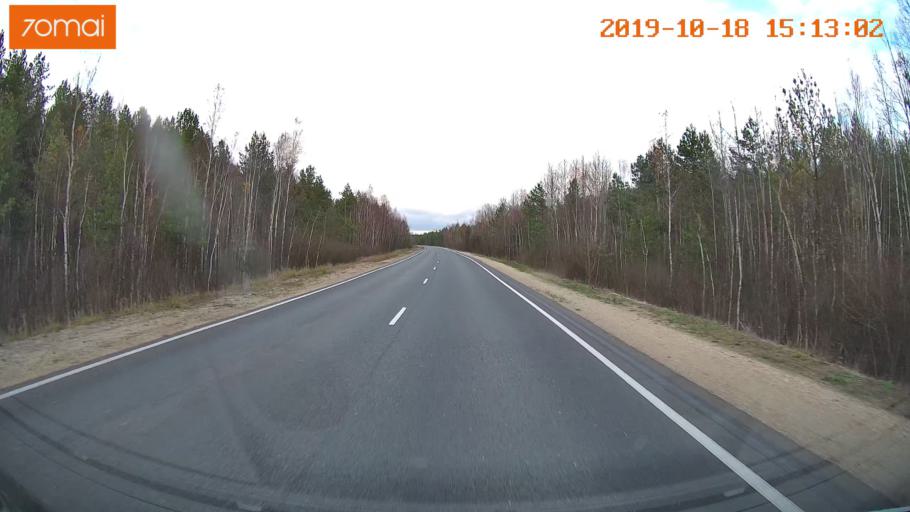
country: RU
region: Vladimir
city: Gus'-Khrustal'nyy
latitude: 55.5813
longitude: 40.7111
